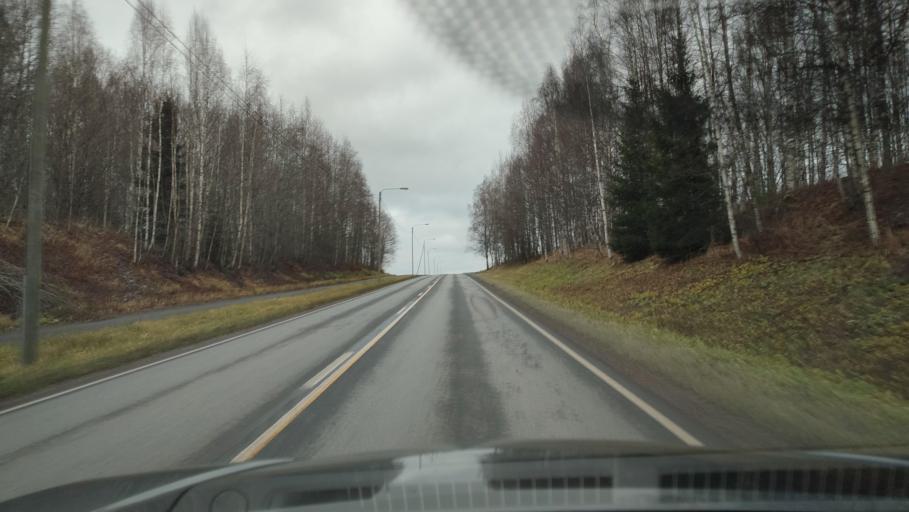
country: FI
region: Southern Ostrobothnia
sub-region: Seinaejoki
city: Kurikka
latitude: 62.5933
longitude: 22.4123
